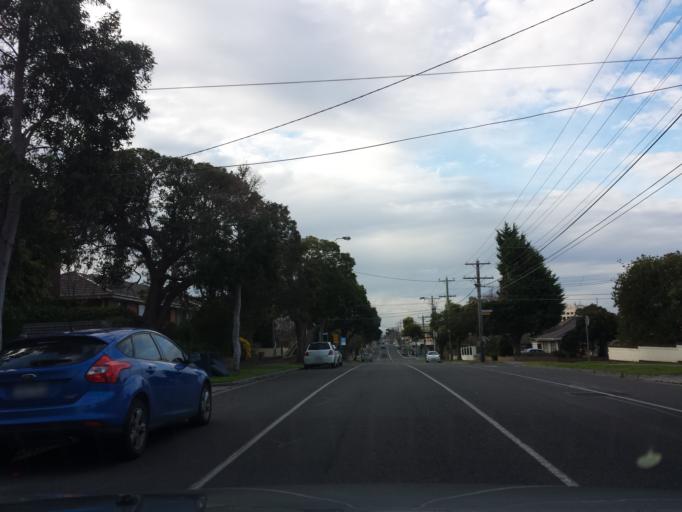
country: AU
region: Victoria
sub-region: Bayside
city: Cheltenham
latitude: -37.9715
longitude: 145.0545
